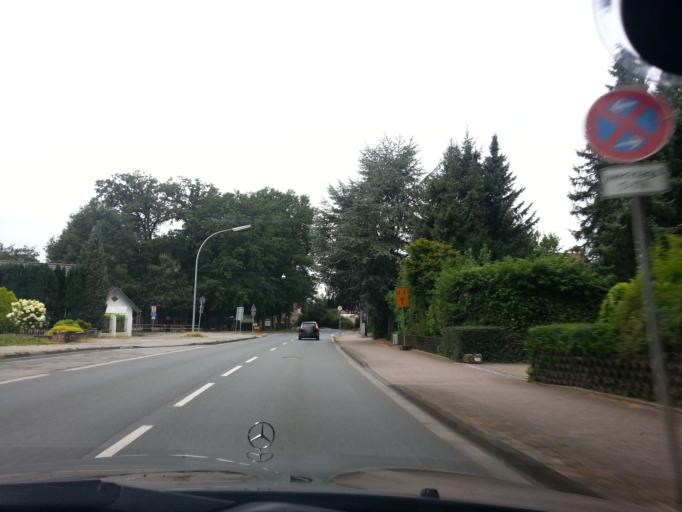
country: DE
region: North Rhine-Westphalia
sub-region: Regierungsbezirk Munster
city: Heiden
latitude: 51.7518
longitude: 6.9302
